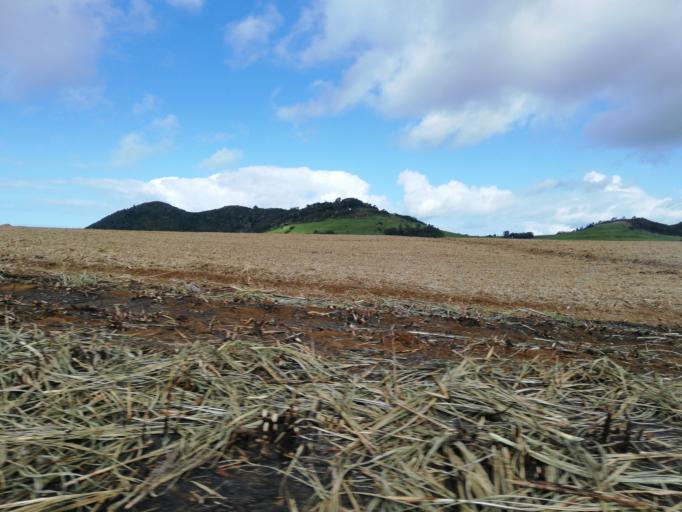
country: MU
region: Flacq
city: Grande Riviere Sud Est
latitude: -20.2842
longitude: 57.7549
